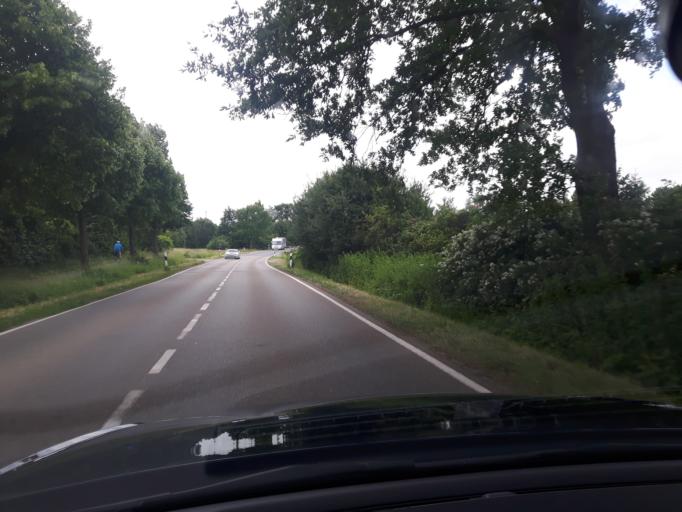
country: DE
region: Schleswig-Holstein
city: Sierksdorf
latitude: 54.0900
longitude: 10.7799
